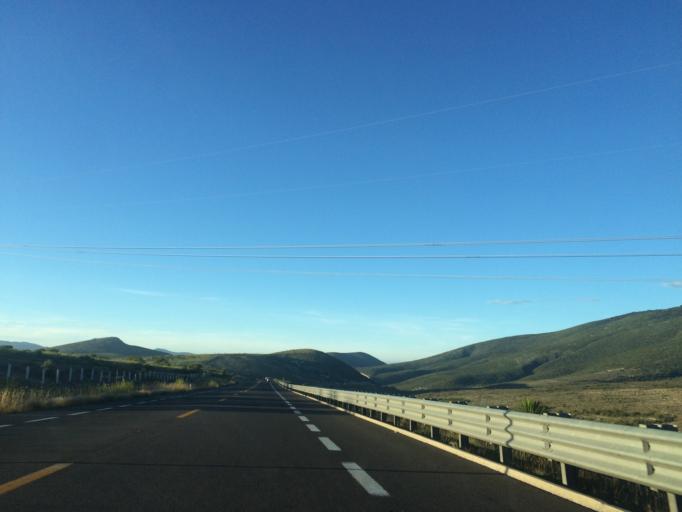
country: MX
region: Puebla
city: Morelos Canada
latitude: 18.6945
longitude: -97.4635
